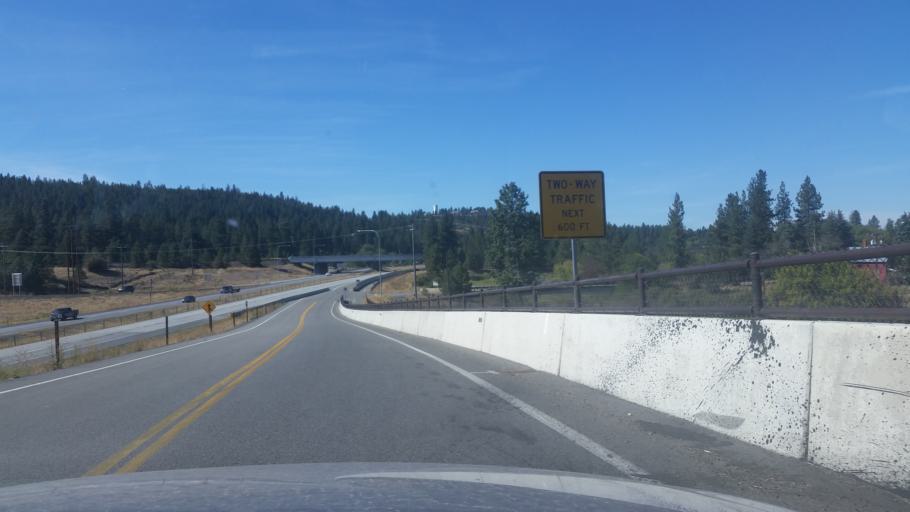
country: US
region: Washington
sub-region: Spokane County
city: Spokane
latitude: 47.6201
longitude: -117.4326
